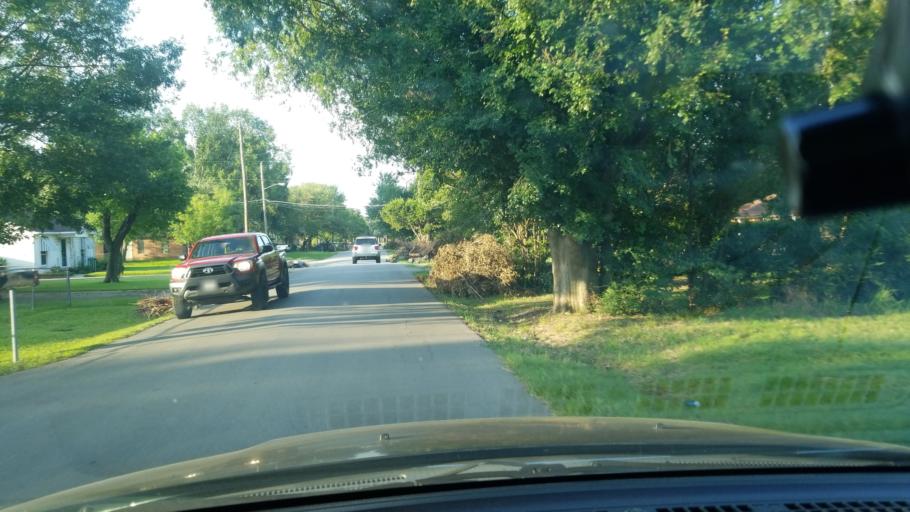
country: US
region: Texas
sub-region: Dallas County
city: Balch Springs
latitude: 32.7223
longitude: -96.6628
